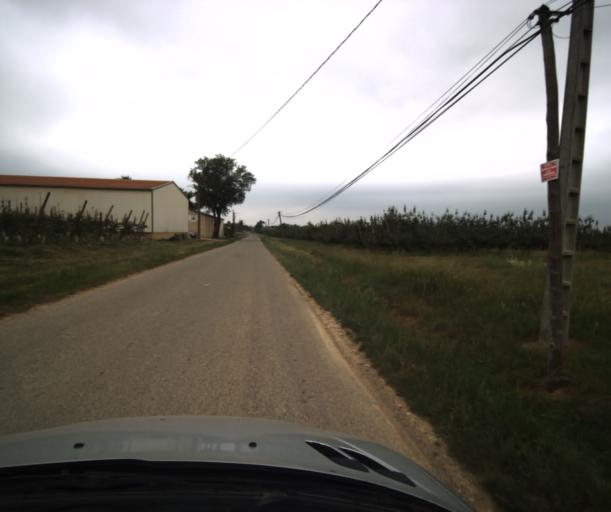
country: FR
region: Midi-Pyrenees
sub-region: Departement du Tarn-et-Garonne
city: Saint-Nicolas-de-la-Grave
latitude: 44.0584
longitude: 0.9820
